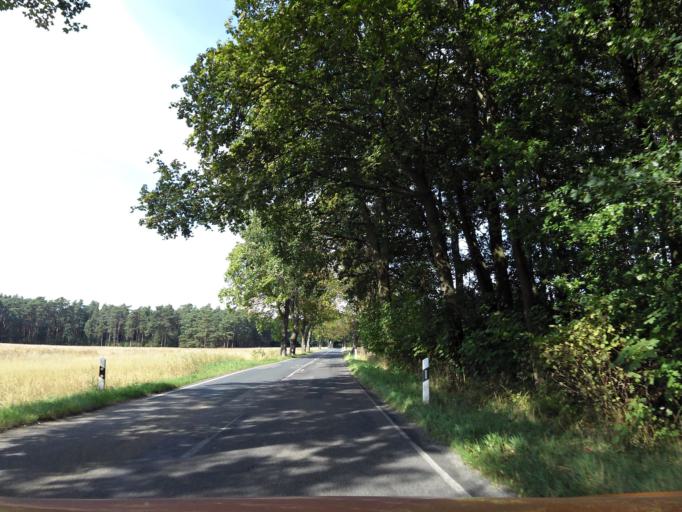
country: DE
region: Brandenburg
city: Michendorf
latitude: 52.2825
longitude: 13.1139
